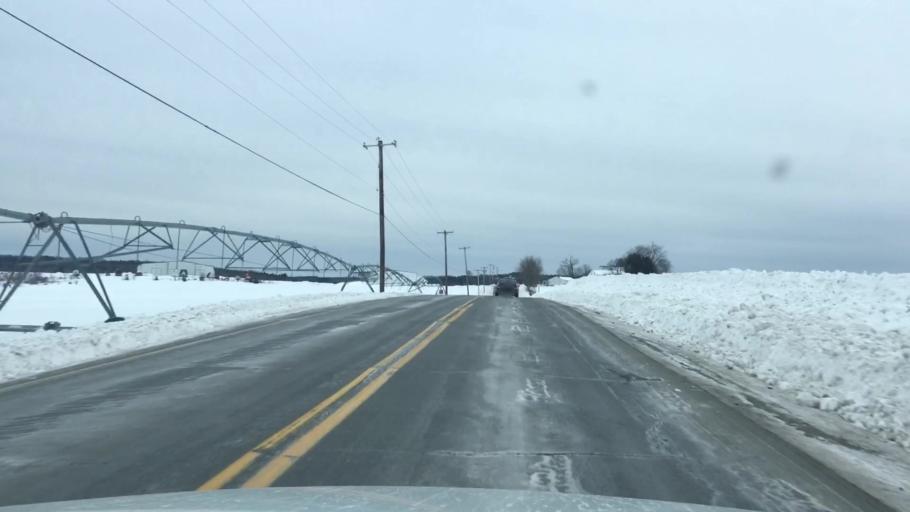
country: US
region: Maine
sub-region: Penobscot County
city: Garland
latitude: 44.9811
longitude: -69.0887
